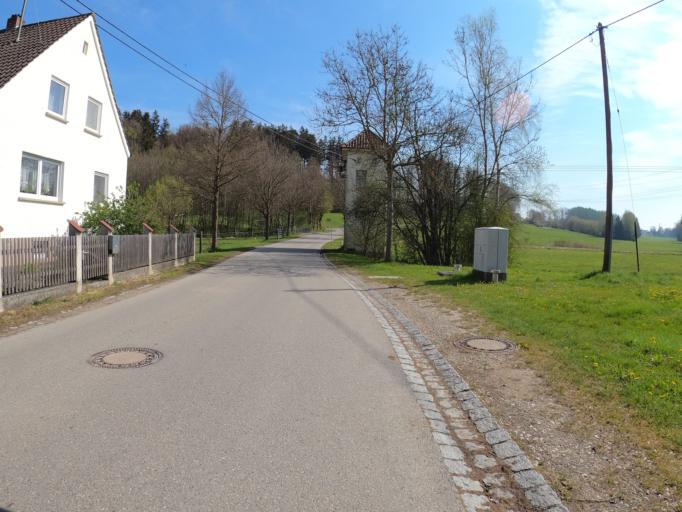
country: DE
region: Bavaria
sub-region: Swabia
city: Pfaffenhofen an der Roth
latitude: 48.3821
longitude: 10.1973
